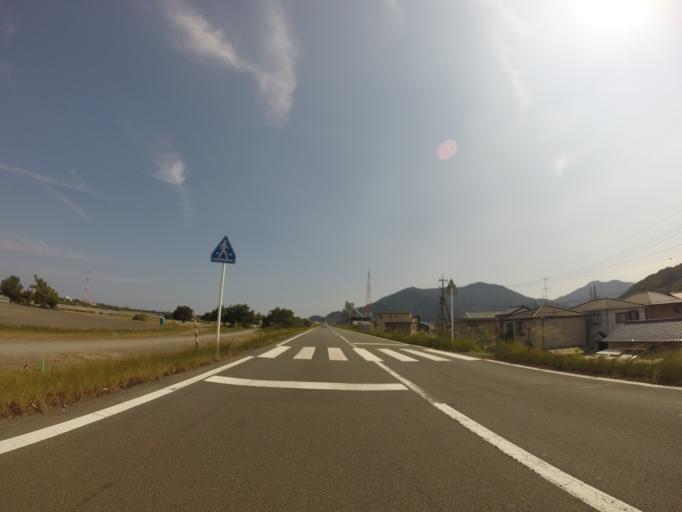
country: JP
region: Shizuoka
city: Shizuoka-shi
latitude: 34.9837
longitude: 138.3550
